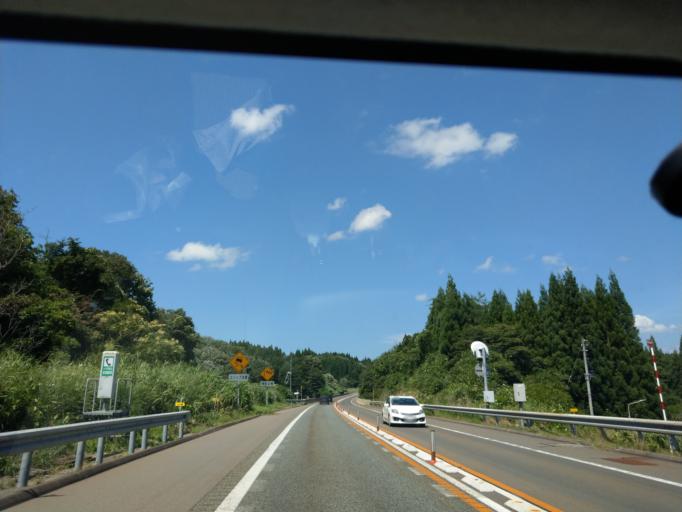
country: JP
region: Akita
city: Akita
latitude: 39.6756
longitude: 140.1863
